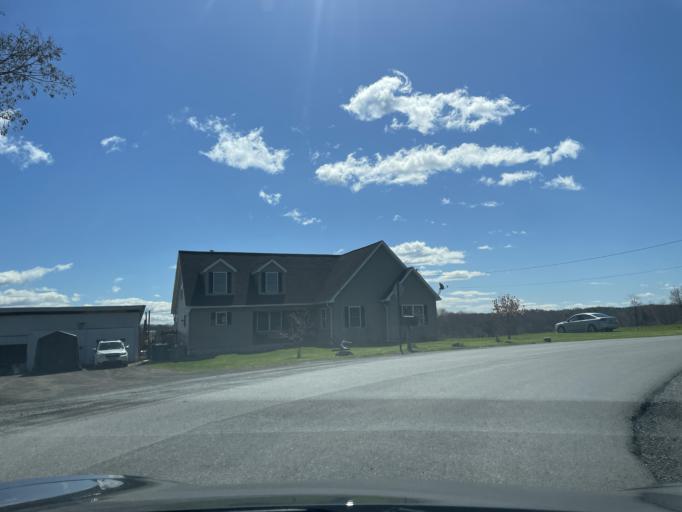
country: US
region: New York
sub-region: Ulster County
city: Saugerties South
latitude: 42.0459
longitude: -73.9913
